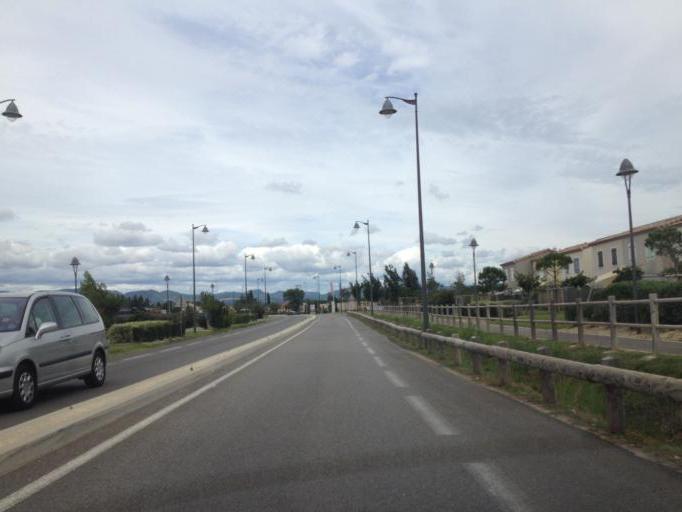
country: FR
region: Rhone-Alpes
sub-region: Departement de la Drome
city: Montelimar
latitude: 44.5356
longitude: 4.7658
